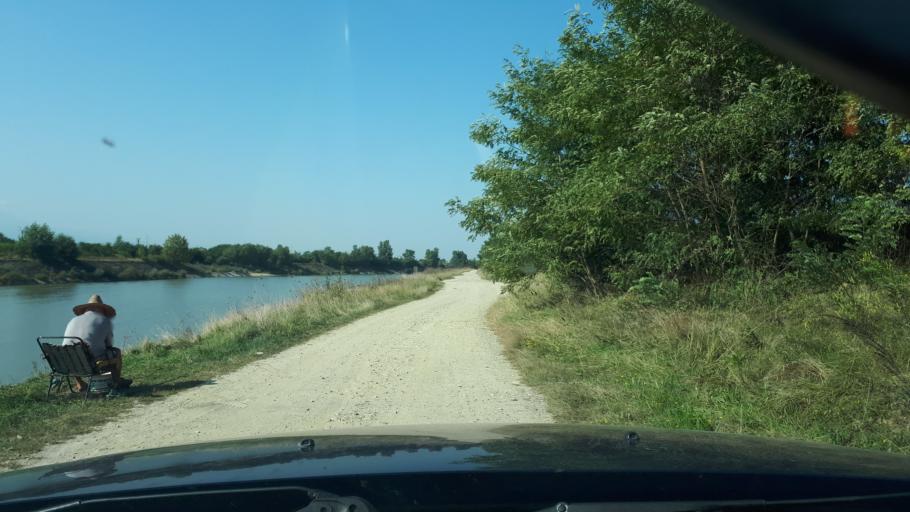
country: RO
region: Brasov
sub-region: Comuna Vistea de Jos
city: Vistea de Jos
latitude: 45.8061
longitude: 24.7393
